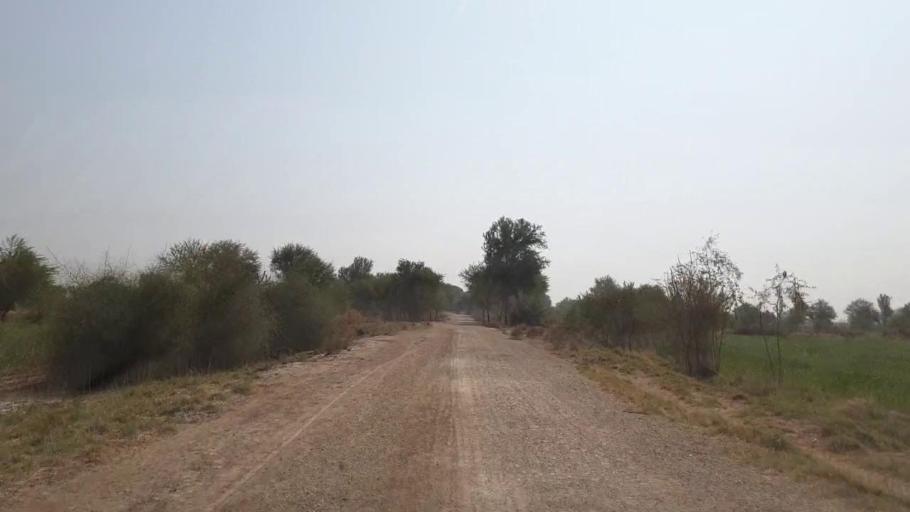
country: PK
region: Sindh
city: Mirpur Khas
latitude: 25.6298
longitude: 69.1451
